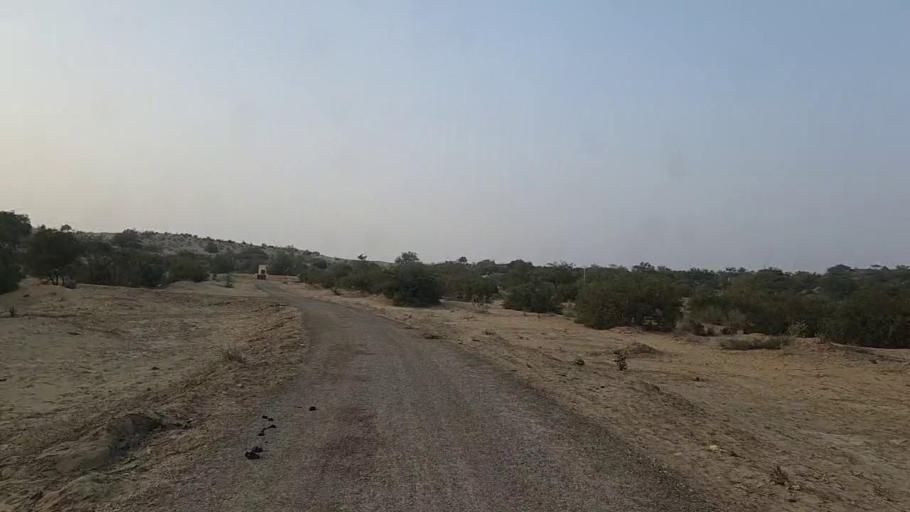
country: PK
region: Sindh
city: Naukot
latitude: 24.6806
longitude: 69.4585
